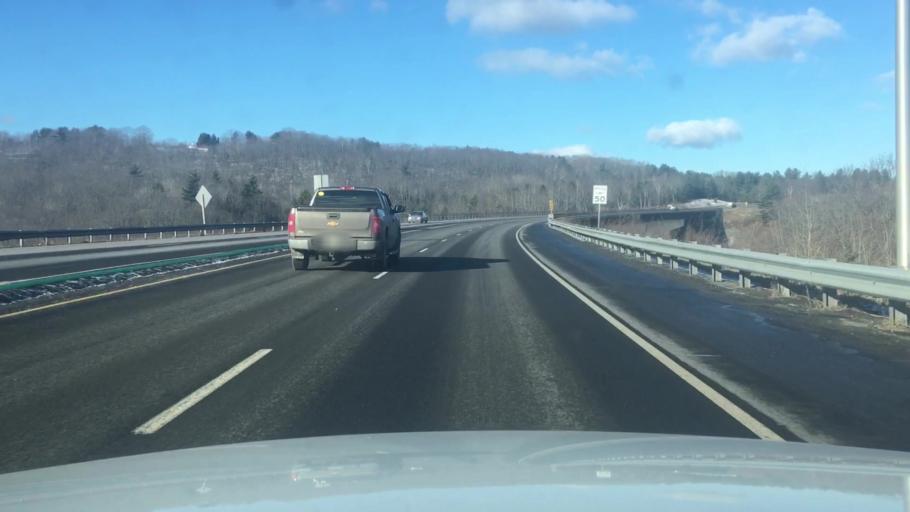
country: US
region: Maine
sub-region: Kennebec County
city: Augusta
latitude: 44.3339
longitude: -69.7622
